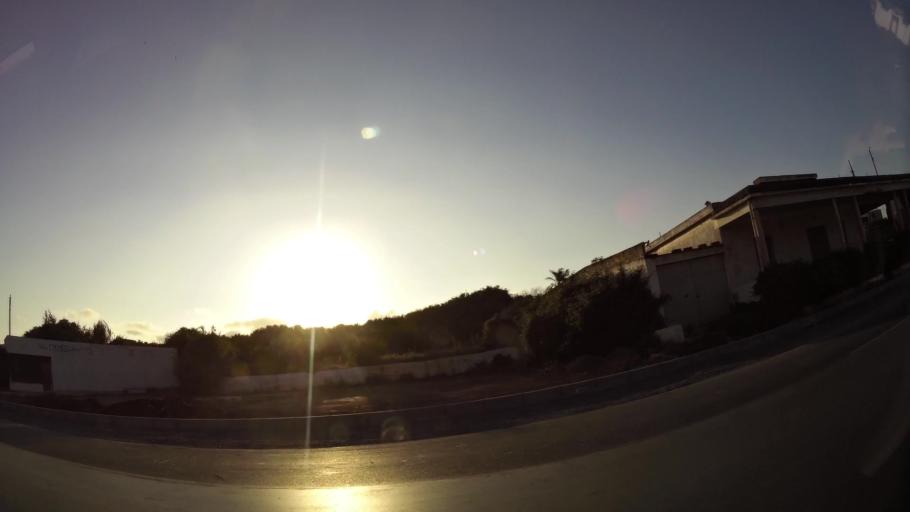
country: MA
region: Rabat-Sale-Zemmour-Zaer
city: Sale
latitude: 34.1230
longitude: -6.7392
